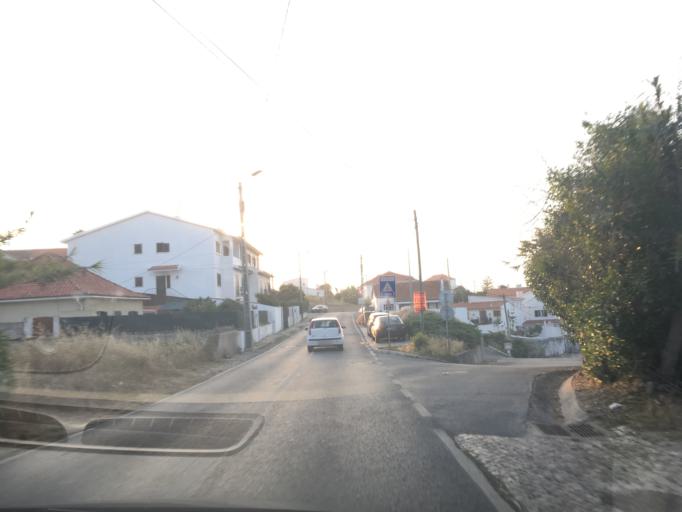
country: PT
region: Lisbon
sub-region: Sintra
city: Colares
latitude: 38.8362
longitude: -9.4583
